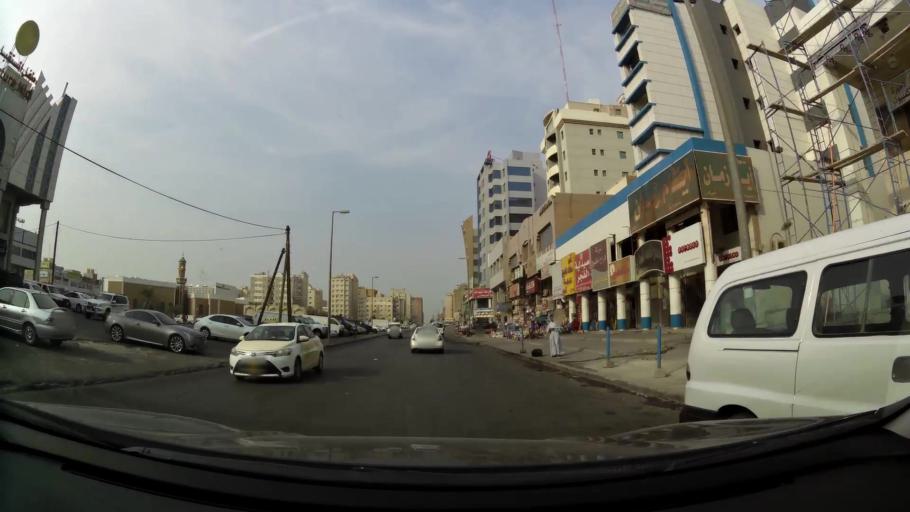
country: KW
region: Al Farwaniyah
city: Al Farwaniyah
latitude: 29.2899
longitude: 47.9746
